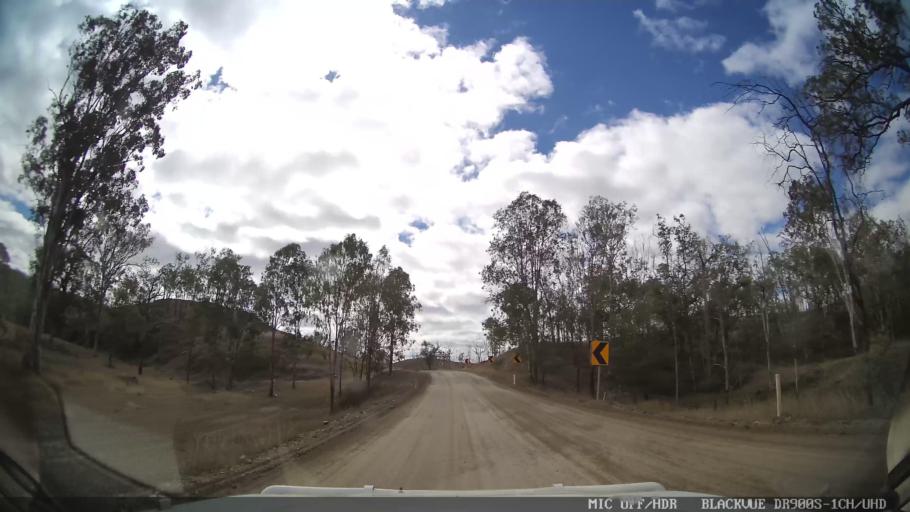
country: AU
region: Queensland
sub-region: Gladstone
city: Toolooa
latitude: -24.6189
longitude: 151.2975
